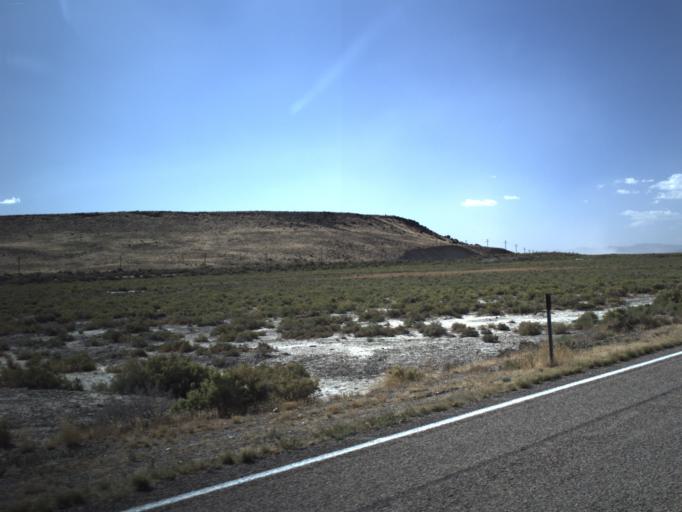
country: US
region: Utah
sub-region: Beaver County
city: Milford
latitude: 38.7388
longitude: -112.9606
